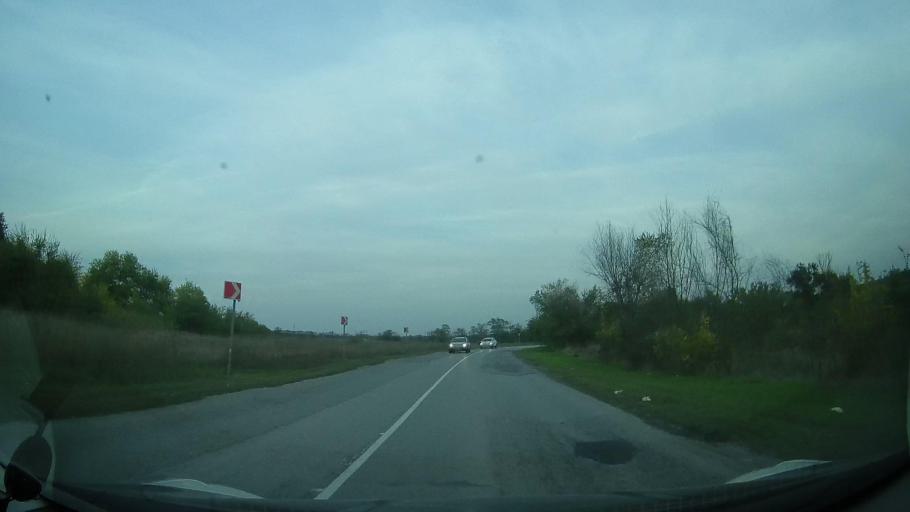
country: RU
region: Rostov
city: Ol'ginskaya
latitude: 47.1195
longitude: 39.9715
